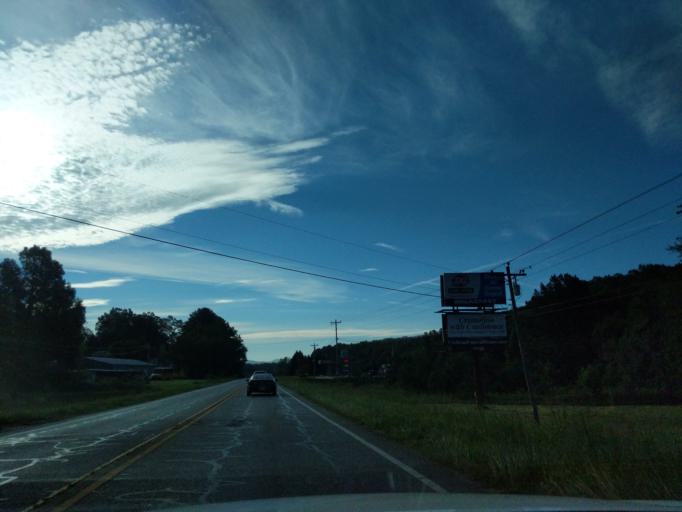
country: US
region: Georgia
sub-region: Fannin County
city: Blue Ridge
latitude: 34.8979
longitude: -84.3630
